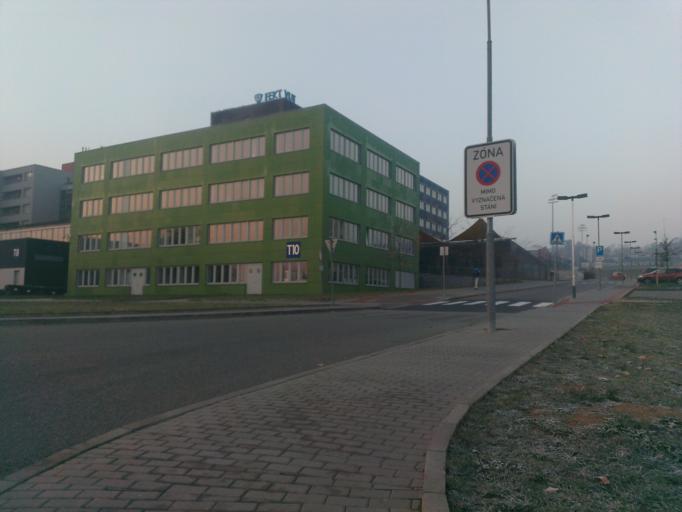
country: CZ
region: South Moravian
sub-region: Mesto Brno
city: Mokra Hora
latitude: 49.2266
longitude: 16.5762
